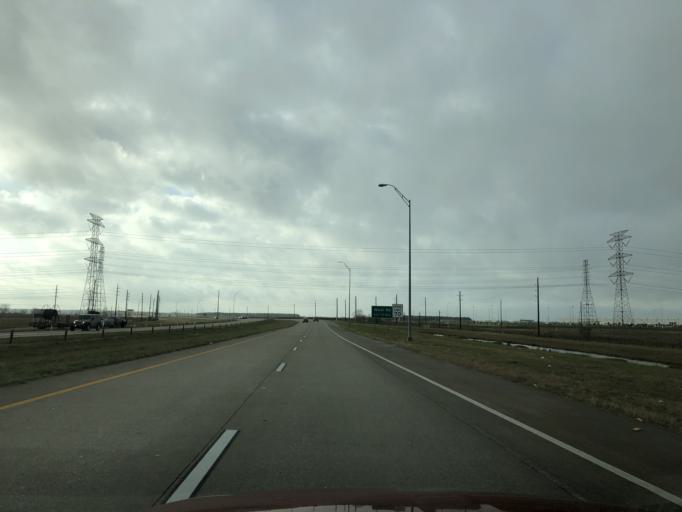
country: US
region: Texas
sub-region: Harris County
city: Cypress
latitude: 29.9152
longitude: -95.7619
